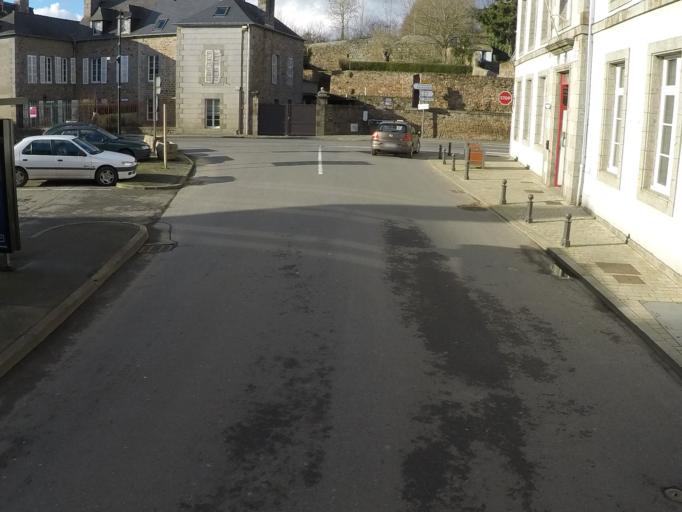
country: FR
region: Brittany
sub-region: Departement des Cotes-d'Armor
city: Plelo
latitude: 48.5426
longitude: -2.9696
